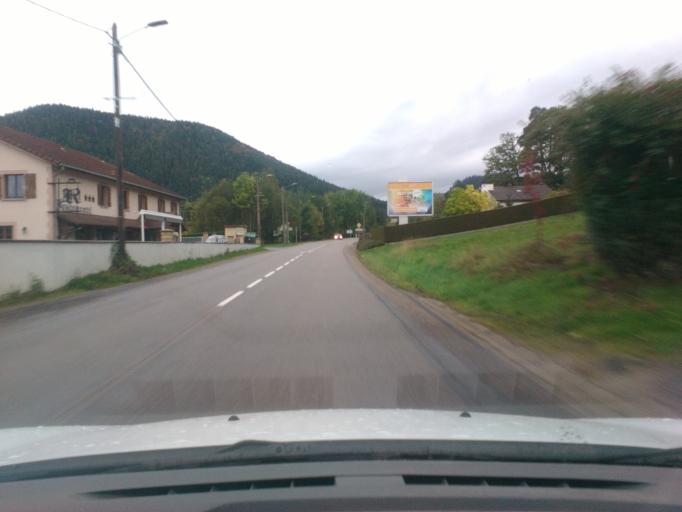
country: FR
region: Lorraine
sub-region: Departement des Vosges
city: Taintrux
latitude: 48.2758
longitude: 6.9009
